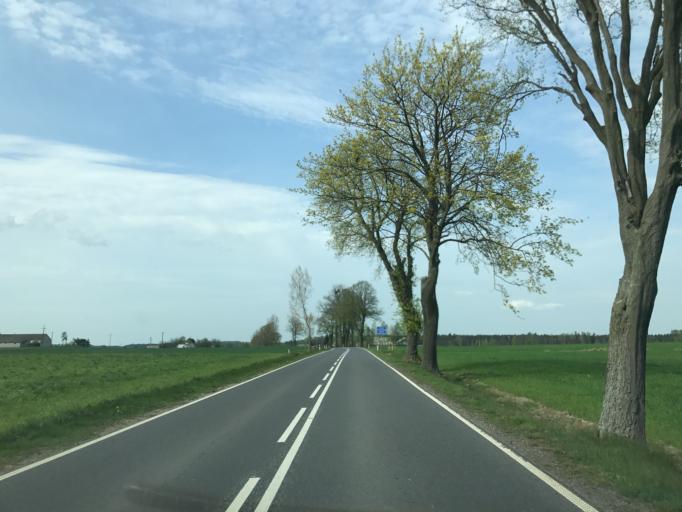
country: PL
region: Warmian-Masurian Voivodeship
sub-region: Powiat dzialdowski
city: Lidzbark
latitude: 53.3525
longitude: 19.8223
